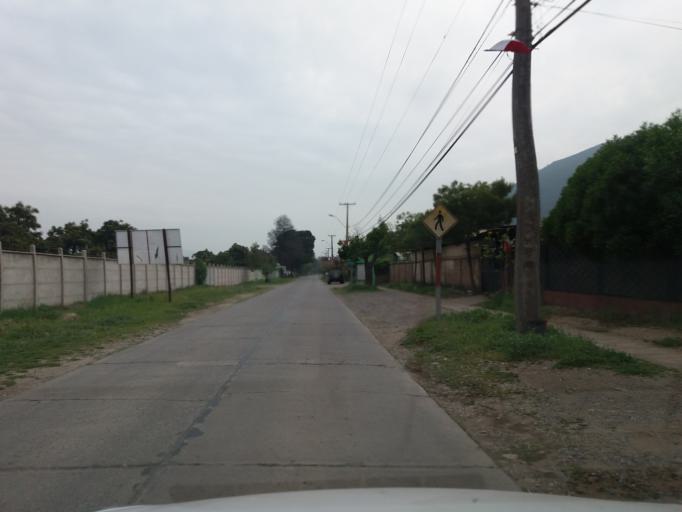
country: CL
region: Valparaiso
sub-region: Provincia de Quillota
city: Hacienda La Calera
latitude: -32.8333
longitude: -71.1160
